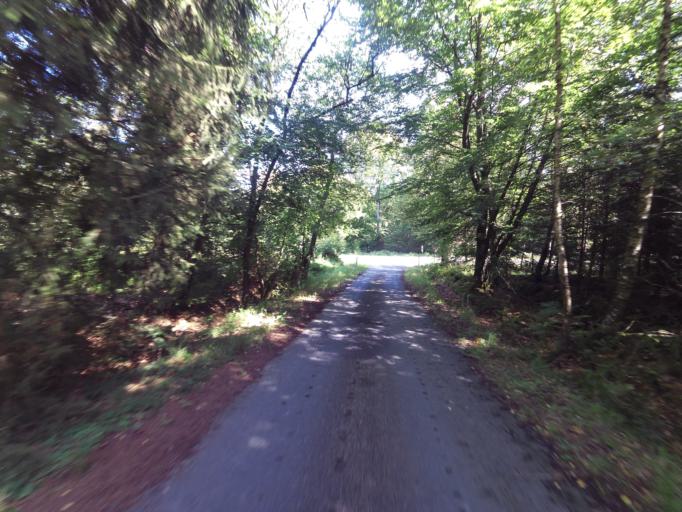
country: BE
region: Wallonia
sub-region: Province du Luxembourg
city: Nassogne
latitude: 50.1121
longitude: 5.3841
